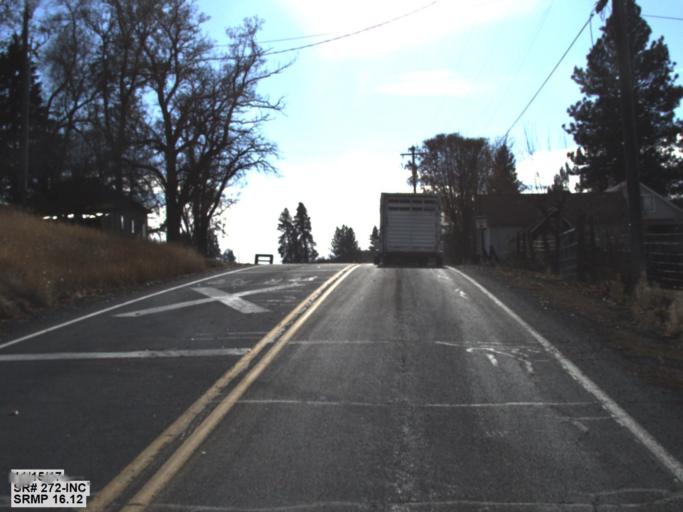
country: US
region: Idaho
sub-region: Latah County
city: Moscow
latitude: 46.9121
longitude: -117.0875
